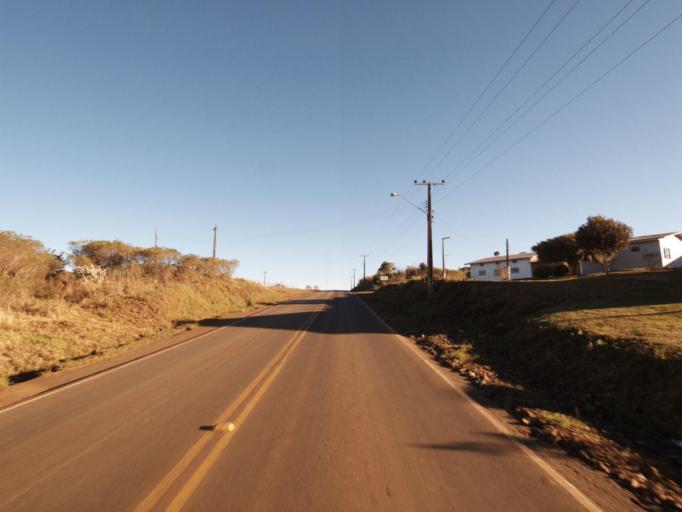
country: AR
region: Misiones
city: Bernardo de Irigoyen
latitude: -26.2684
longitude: -53.6362
